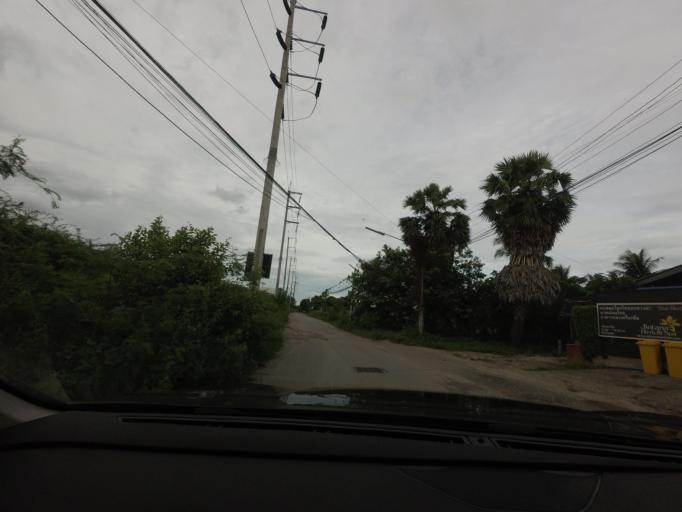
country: TH
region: Prachuap Khiri Khan
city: Hua Hin
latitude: 12.5372
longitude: 99.9467
